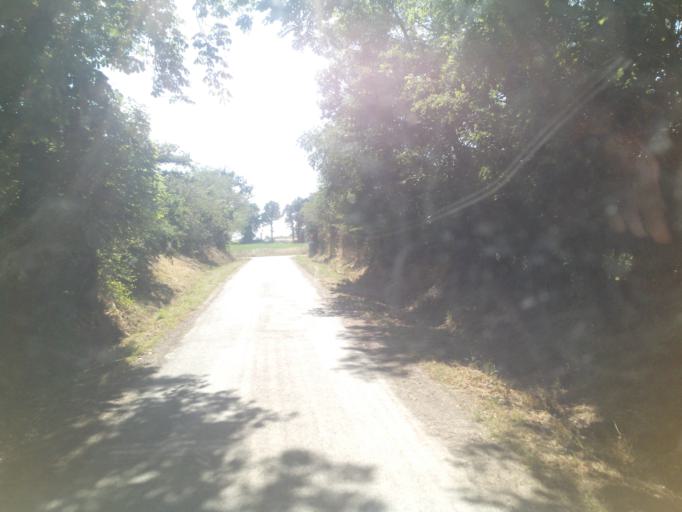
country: FR
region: Brittany
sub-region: Departement du Morbihan
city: Campeneac
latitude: 47.9750
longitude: -2.2751
